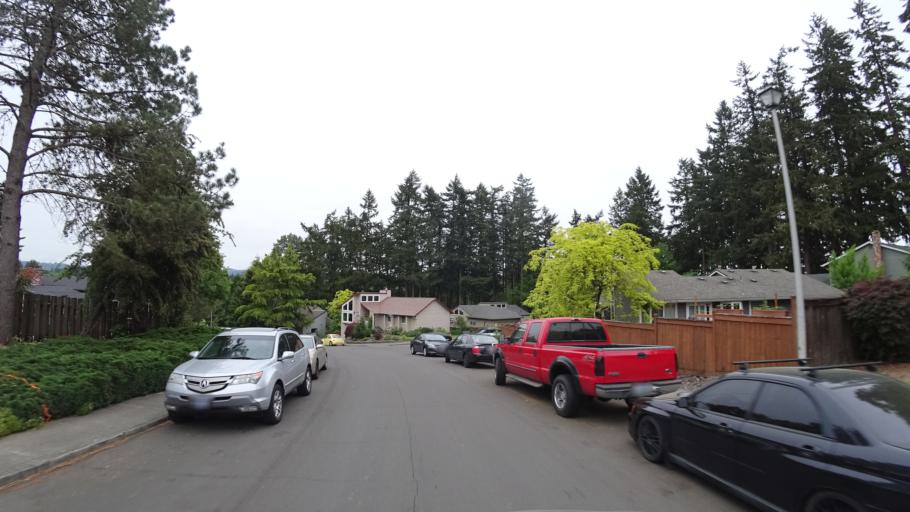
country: US
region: Oregon
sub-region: Washington County
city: Bethany
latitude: 45.5529
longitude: -122.8647
